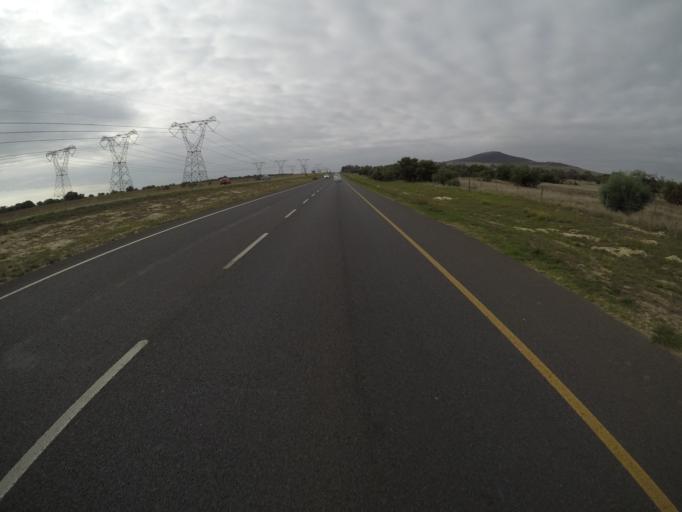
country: ZA
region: Western Cape
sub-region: City of Cape Town
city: Sunset Beach
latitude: -33.7383
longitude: 18.5456
